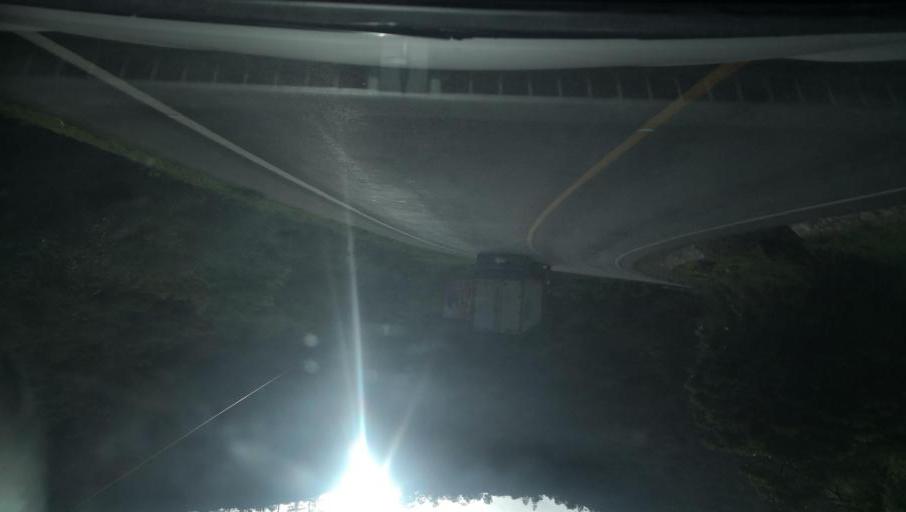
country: NI
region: Nueva Segovia
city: Mozonte
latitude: 13.7118
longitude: -86.5012
